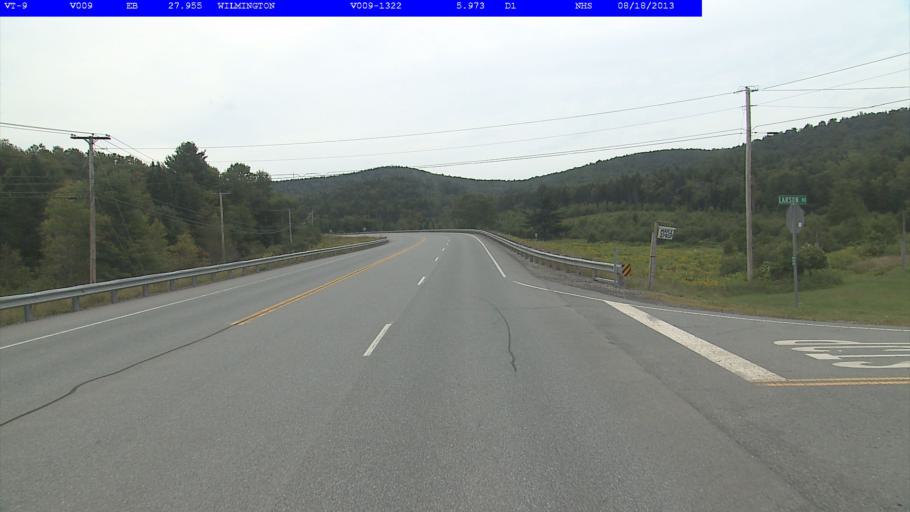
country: US
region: Vermont
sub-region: Windham County
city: Dover
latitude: 42.8553
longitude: -72.8223
